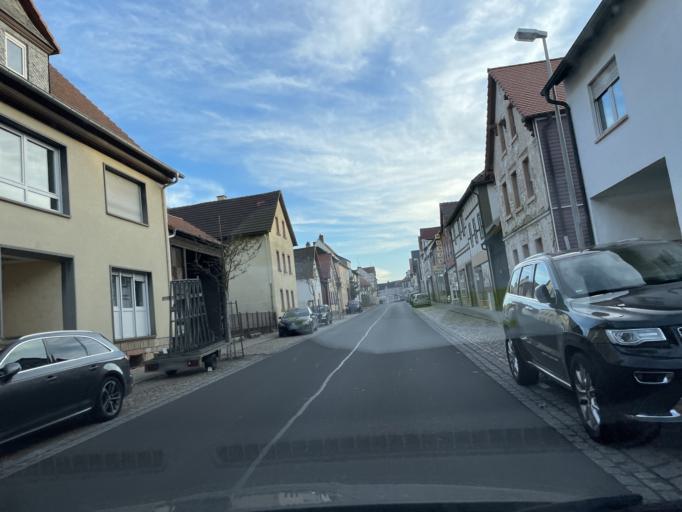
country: DE
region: Bavaria
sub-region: Regierungsbezirk Unterfranken
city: Grossostheim
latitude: 49.9233
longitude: 9.0737
